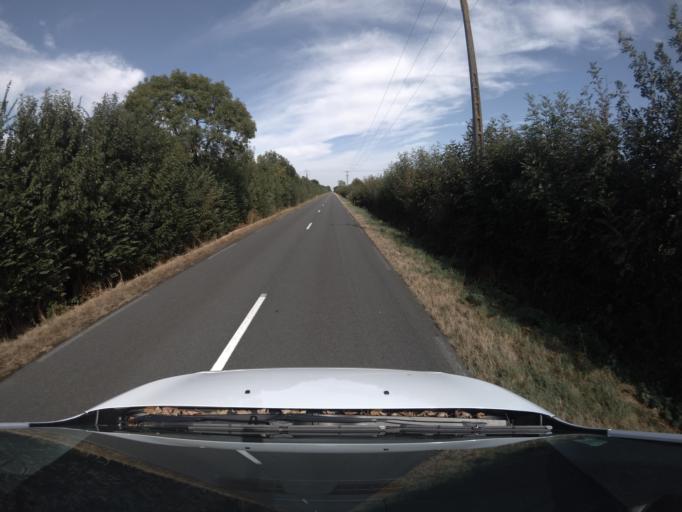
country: FR
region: Poitou-Charentes
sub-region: Departement des Deux-Sevres
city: Argenton-les-Vallees
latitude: 46.9828
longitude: -0.4776
